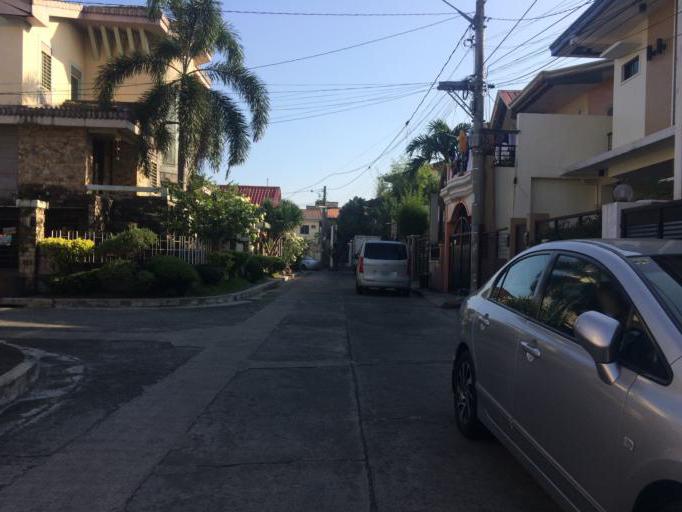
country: PH
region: Calabarzon
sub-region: Province of Rizal
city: Taytay
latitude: 14.5540
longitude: 121.1068
